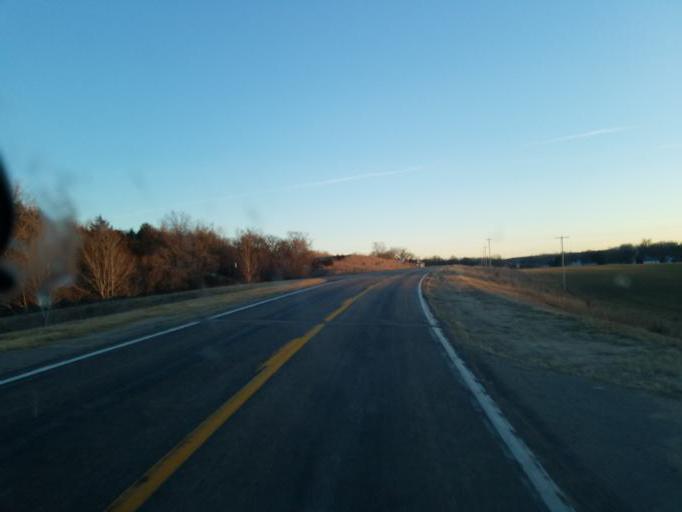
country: US
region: Nebraska
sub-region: Knox County
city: Center
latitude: 42.6156
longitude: -97.8782
